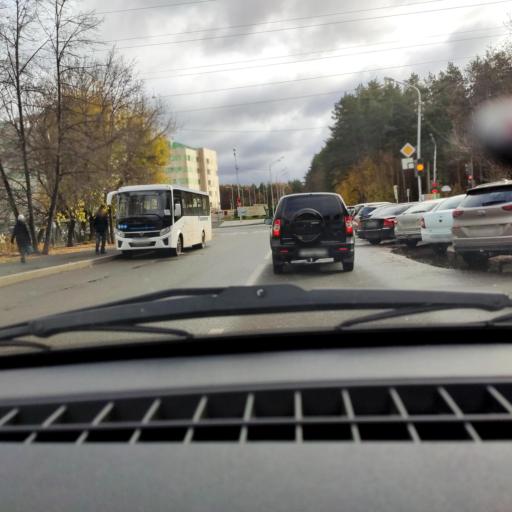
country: RU
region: Bashkortostan
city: Ufa
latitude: 54.7076
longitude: 56.0078
